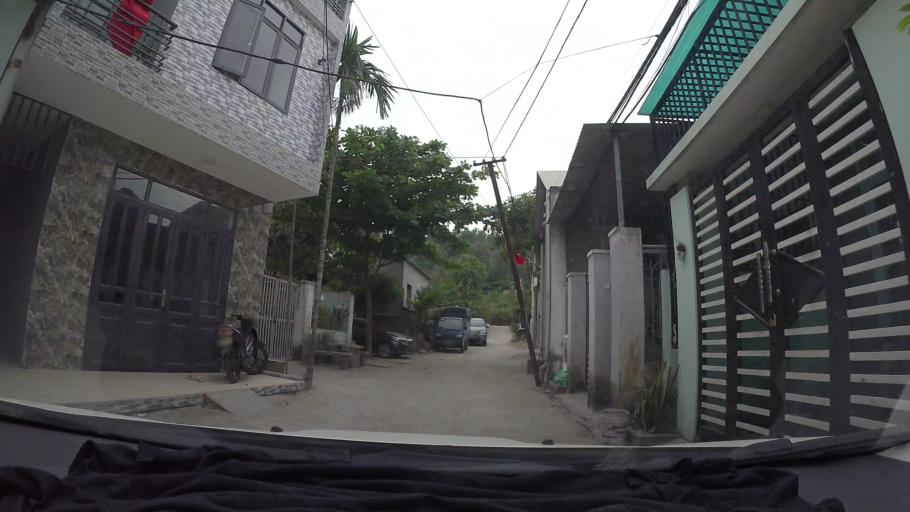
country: VN
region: Da Nang
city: Lien Chieu
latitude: 16.0402
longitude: 108.1711
